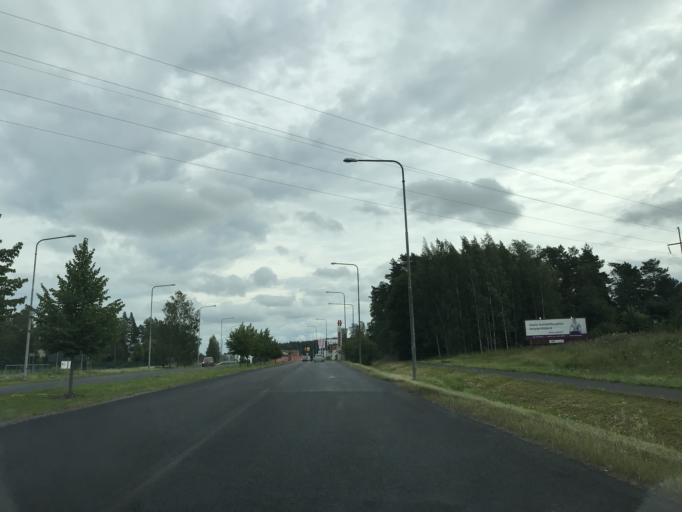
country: FI
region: Varsinais-Suomi
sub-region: Turku
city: Kaarina
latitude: 60.4101
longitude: 22.3573
